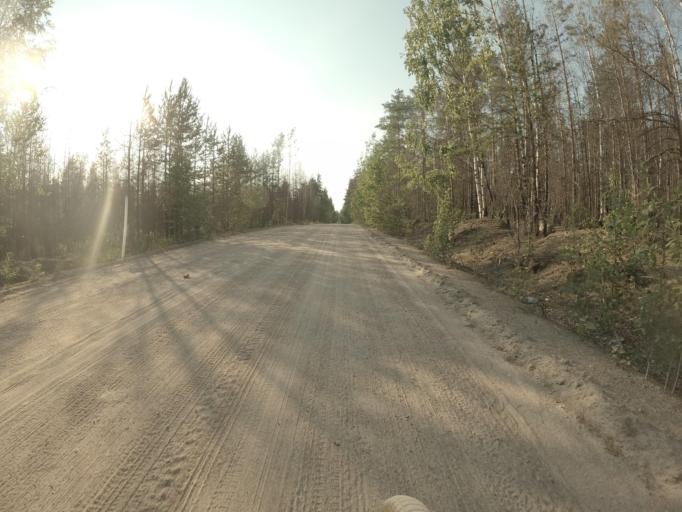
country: RU
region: Leningrad
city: Veshchevo
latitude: 60.4587
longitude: 29.2462
